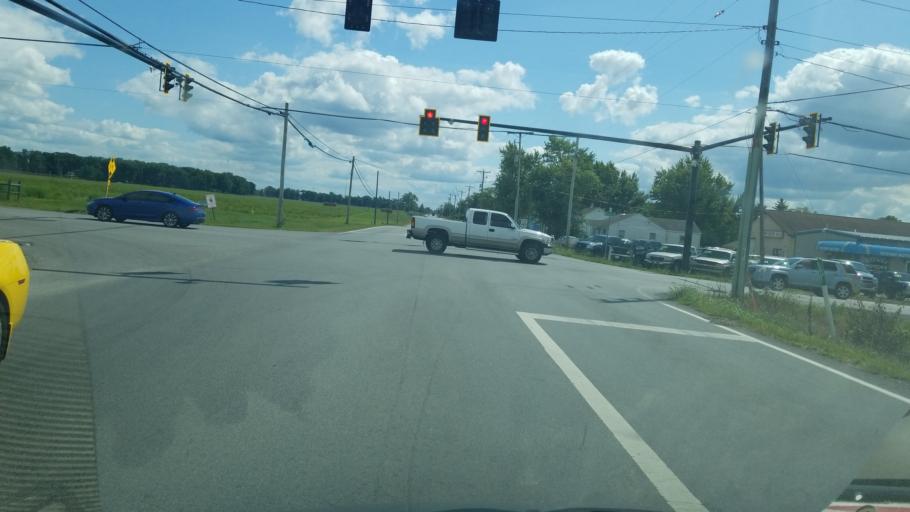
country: US
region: Ohio
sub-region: Allen County
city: Lima
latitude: 40.7885
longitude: -84.1088
